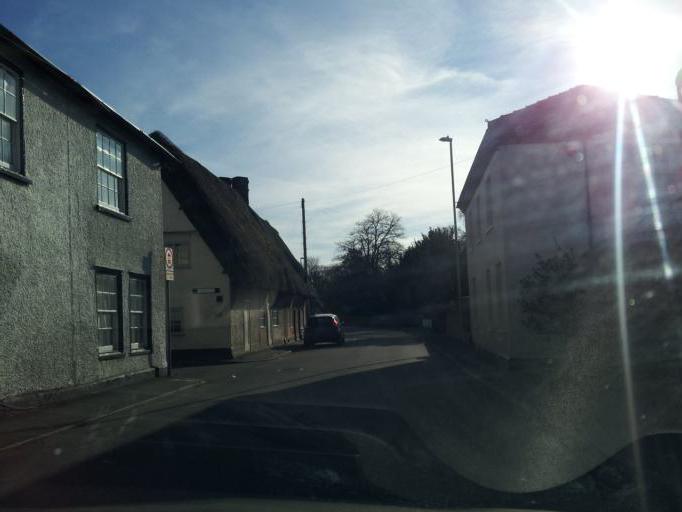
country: GB
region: England
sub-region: Cambridgeshire
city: Melbourn
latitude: 52.0821
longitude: 0.0148
